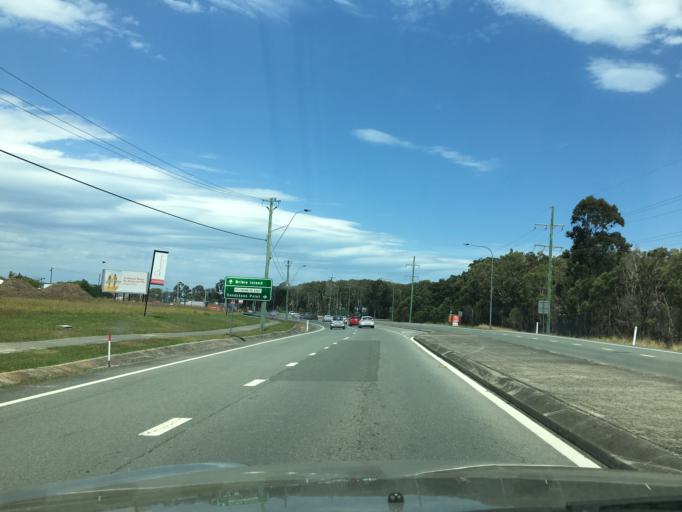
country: AU
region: Queensland
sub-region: Moreton Bay
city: Bongaree
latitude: -27.0733
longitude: 153.1361
